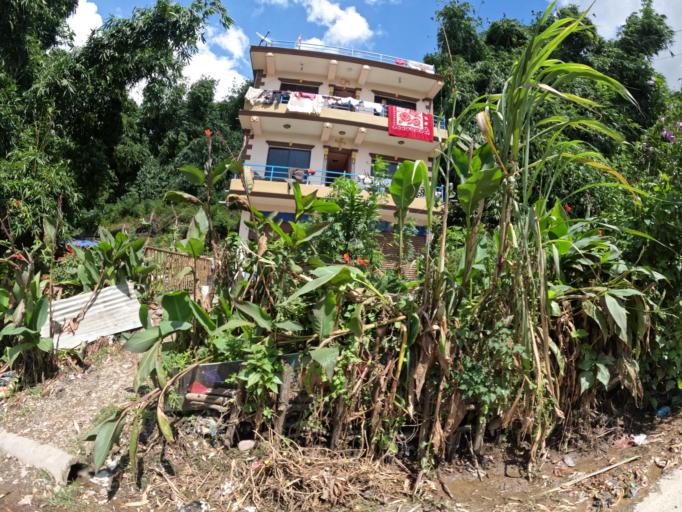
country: NP
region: Central Region
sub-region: Bagmati Zone
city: Kathmandu
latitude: 27.7693
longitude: 85.3274
